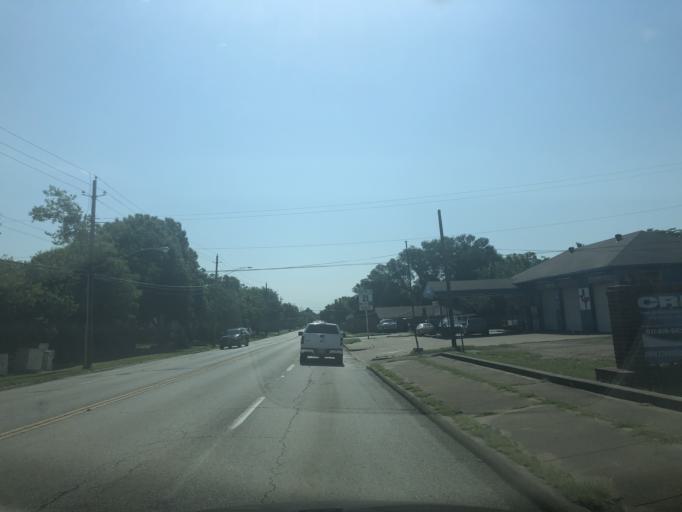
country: US
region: Texas
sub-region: Dallas County
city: Grand Prairie
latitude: 32.7204
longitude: -97.0128
